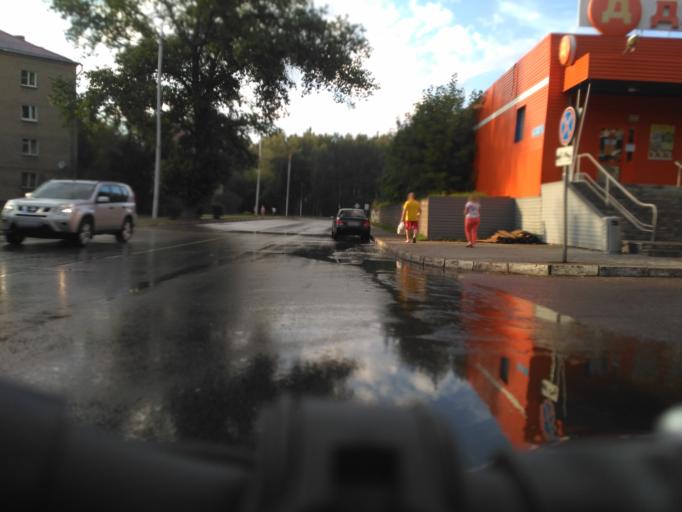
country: RU
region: Moskovskaya
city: Dubna
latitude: 56.7517
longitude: 37.2028
